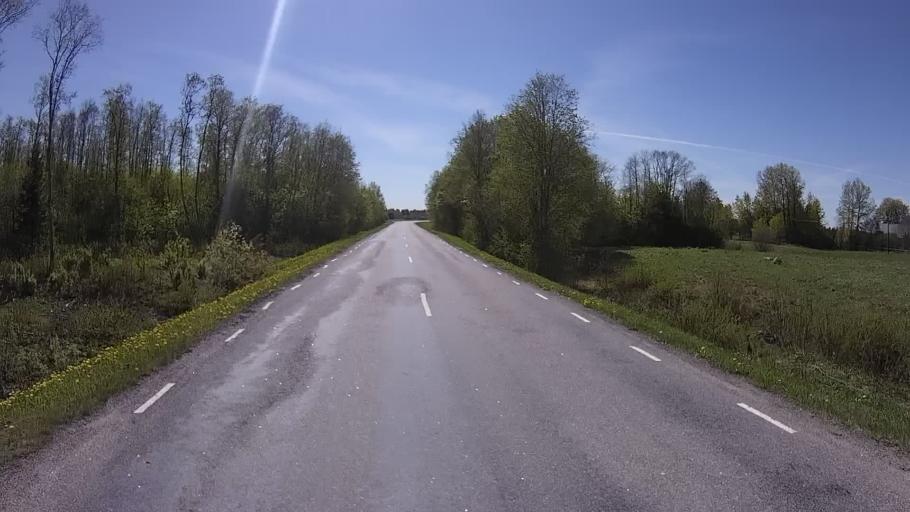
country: EE
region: Harju
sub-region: Rae vald
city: Vaida
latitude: 59.0679
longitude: 25.1557
